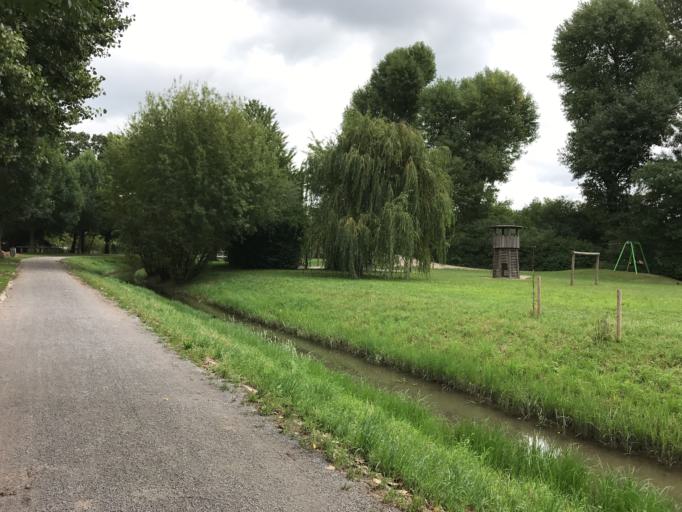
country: DE
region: Baden-Wuerttemberg
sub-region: Karlsruhe Region
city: Karlsruhe
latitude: 49.0270
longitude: 8.4575
